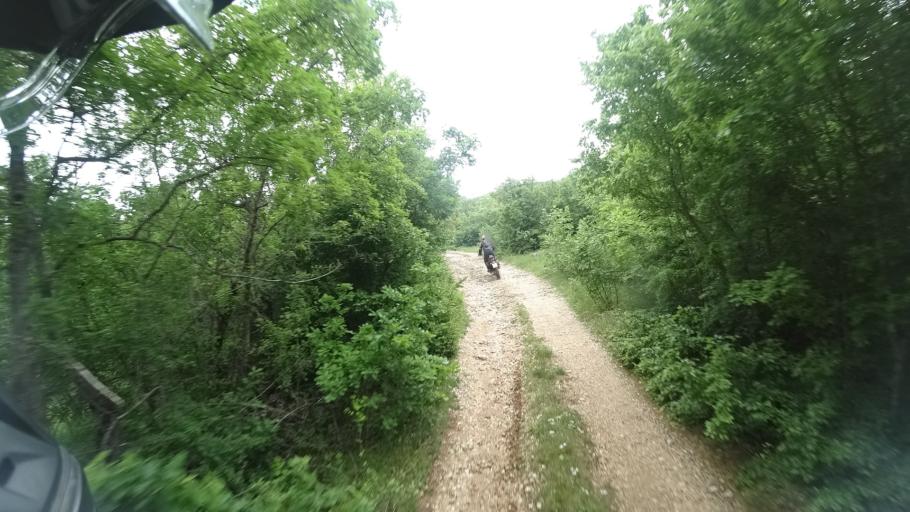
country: HR
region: Splitsko-Dalmatinska
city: Hrvace
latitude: 43.8932
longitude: 16.5317
